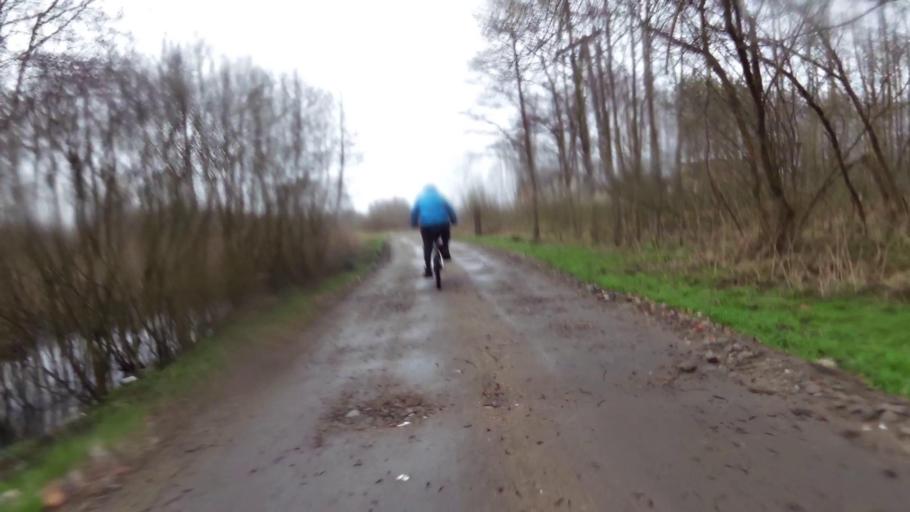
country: PL
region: West Pomeranian Voivodeship
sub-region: Powiat kolobrzeski
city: Grzybowo
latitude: 54.1590
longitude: 15.5004
